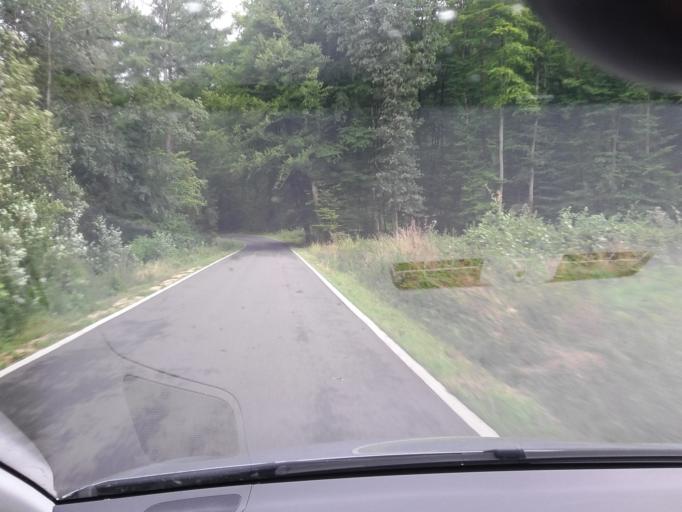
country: BE
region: Wallonia
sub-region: Province du Luxembourg
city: Arlon
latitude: 49.7194
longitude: 5.8181
